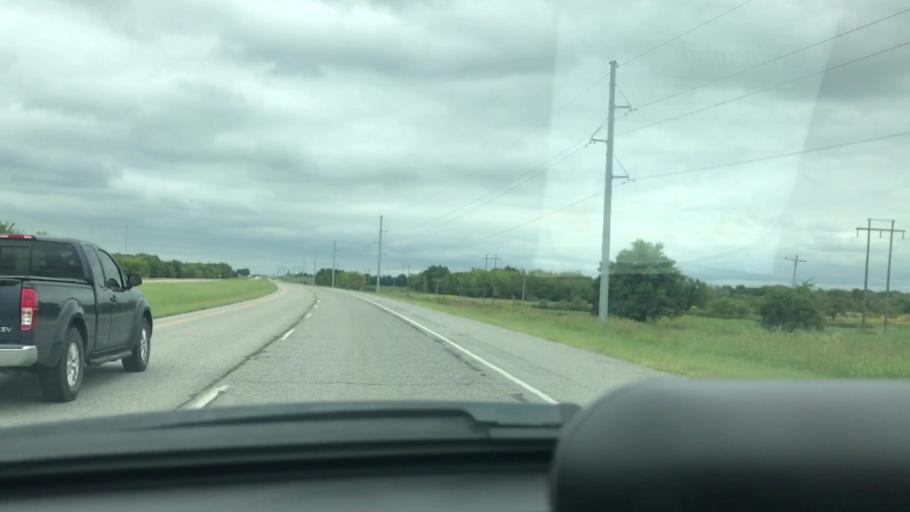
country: US
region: Oklahoma
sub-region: Wagoner County
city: Wagoner
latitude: 35.9983
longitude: -95.3686
